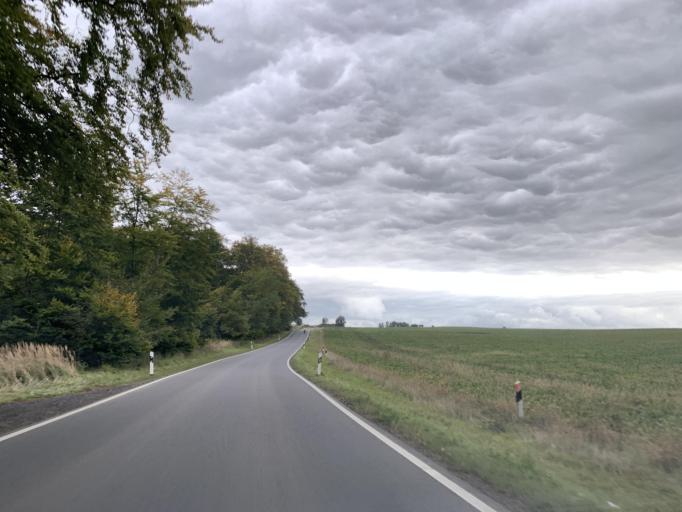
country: DE
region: Mecklenburg-Vorpommern
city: Burg Stargard
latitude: 53.4737
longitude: 13.2924
